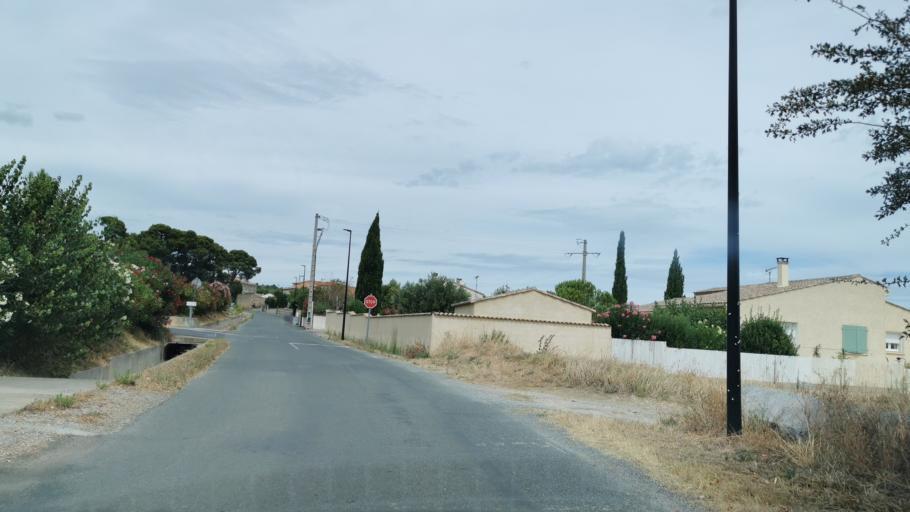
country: FR
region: Languedoc-Roussillon
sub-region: Departement de l'Aude
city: Bize-Minervois
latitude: 43.2998
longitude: 2.8278
